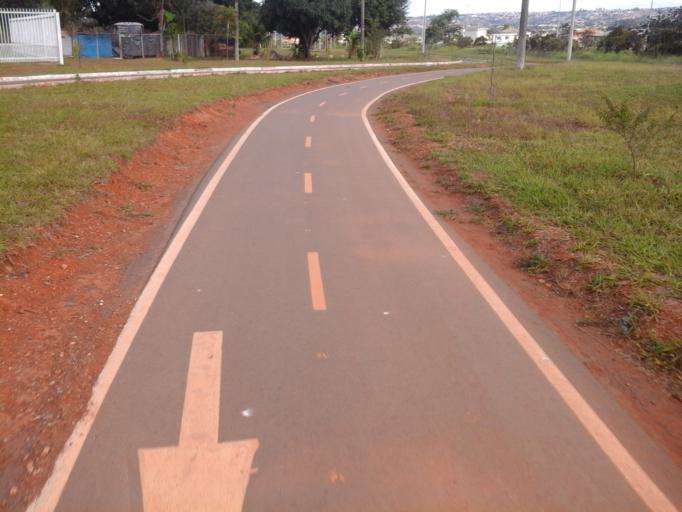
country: BR
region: Federal District
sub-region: Brasilia
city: Brasilia
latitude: -15.8149
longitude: -47.9923
